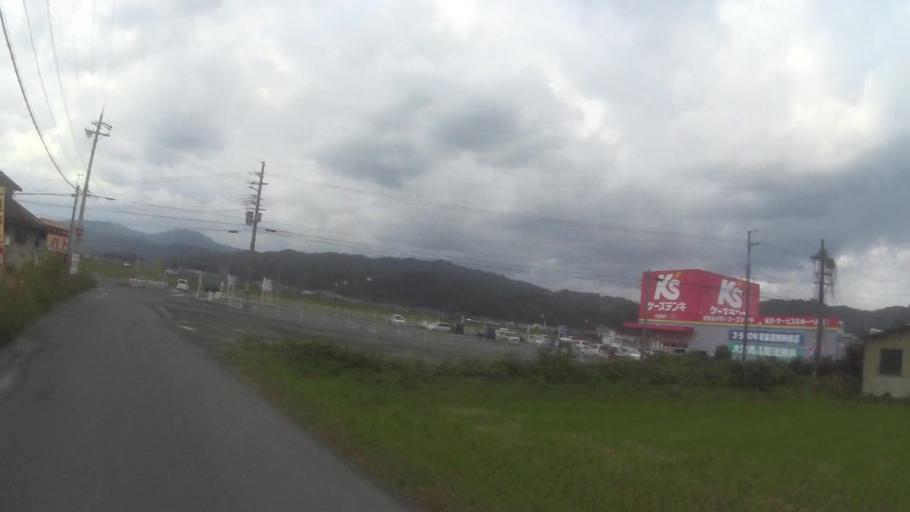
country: JP
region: Kyoto
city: Miyazu
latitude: 35.5280
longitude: 135.1209
